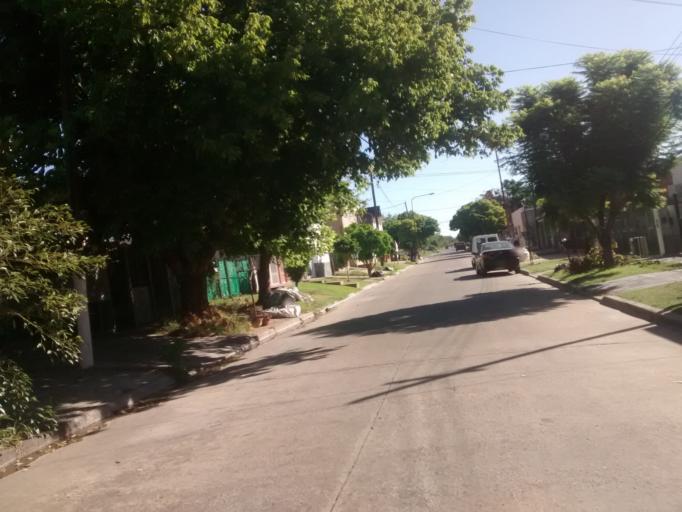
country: AR
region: Buenos Aires
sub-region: Partido de La Plata
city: La Plata
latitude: -34.9239
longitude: -57.9129
